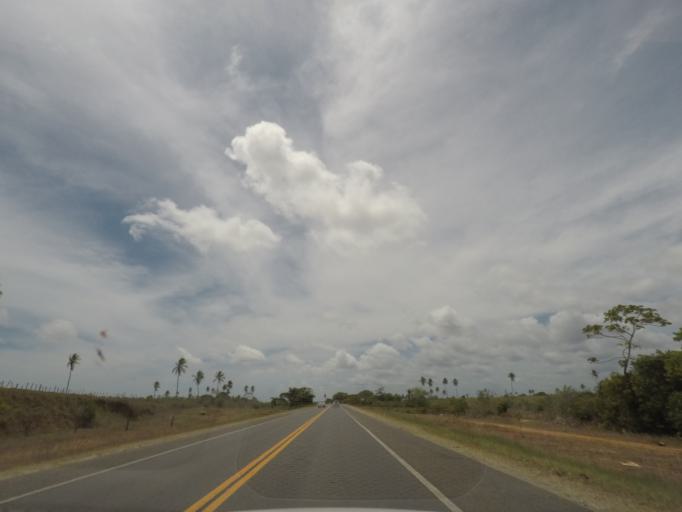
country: BR
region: Bahia
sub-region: Conde
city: Conde
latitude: -11.8124
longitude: -37.6337
